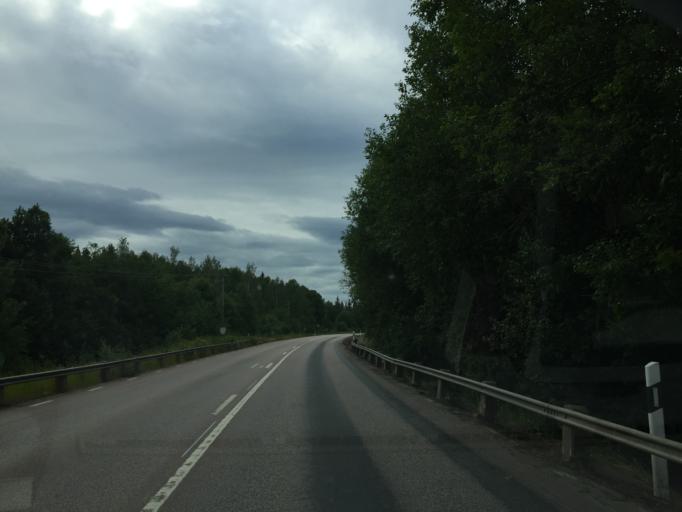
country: SE
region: Vaestmanland
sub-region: Norbergs Kommun
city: Norberg
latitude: 60.0365
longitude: 15.9710
